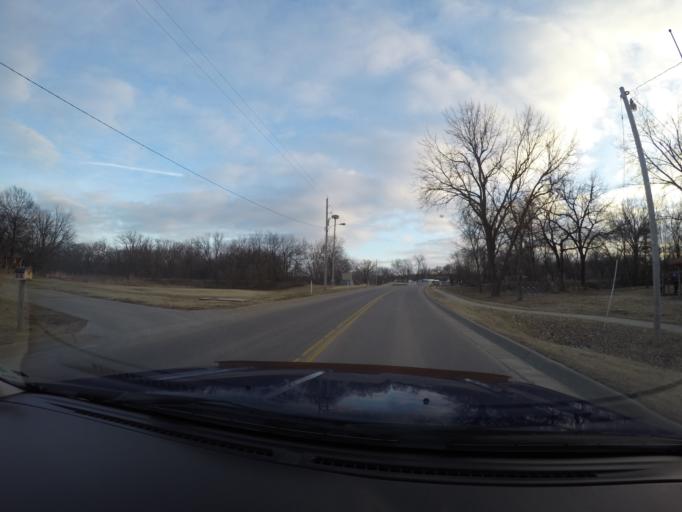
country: US
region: Kansas
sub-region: Morris County
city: Council Grove
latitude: 38.6559
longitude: -96.4882
